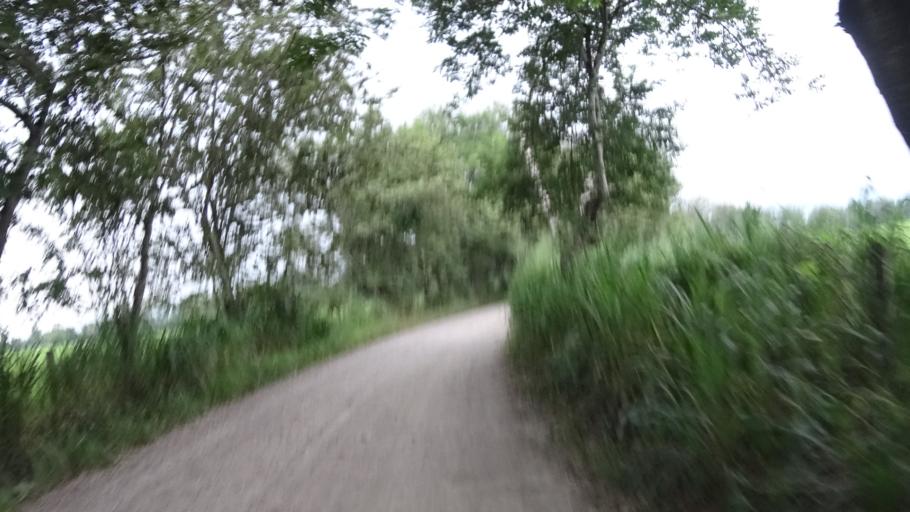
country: CO
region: Cundinamarca
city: Puerto Salgar
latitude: 5.4866
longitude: -74.6909
